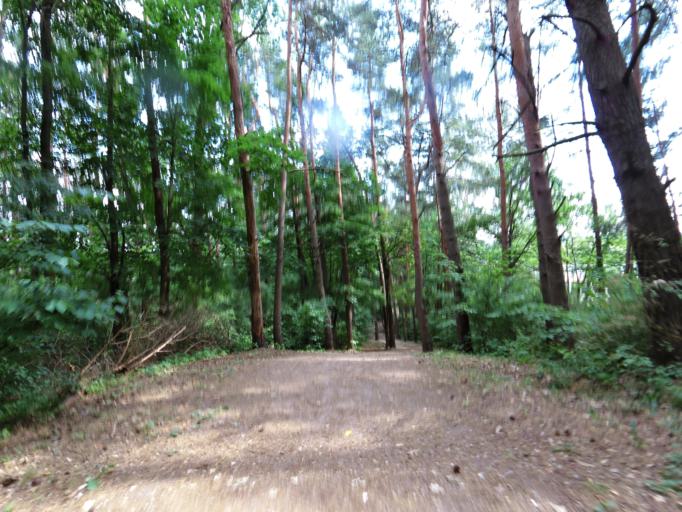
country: LT
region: Vilnius County
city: Lazdynai
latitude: 54.6859
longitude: 25.2167
